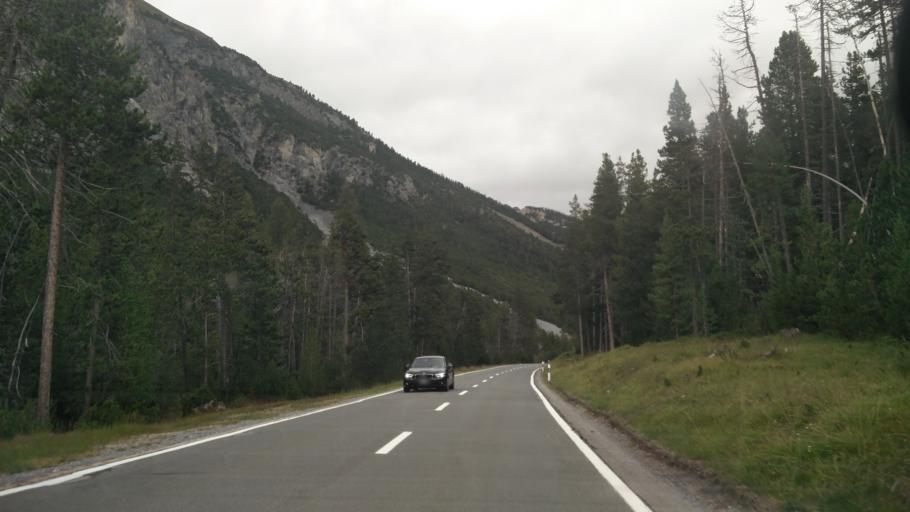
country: CH
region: Grisons
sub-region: Inn District
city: Zernez
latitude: 46.6631
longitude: 10.2013
